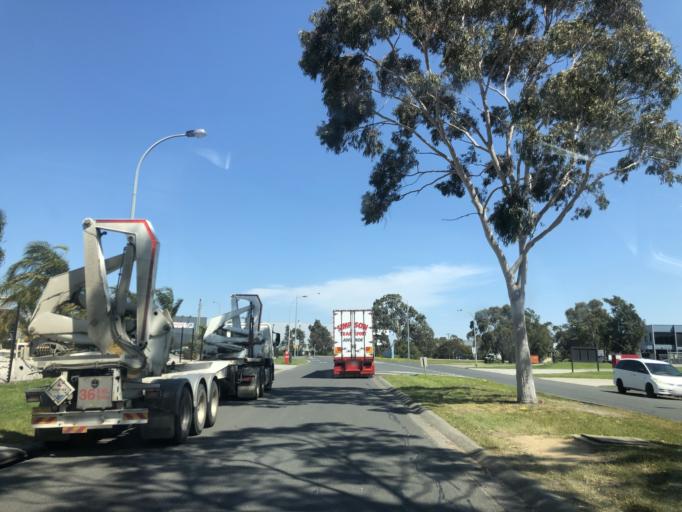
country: AU
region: Victoria
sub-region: Casey
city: Hampton Park
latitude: -38.0324
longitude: 145.2283
